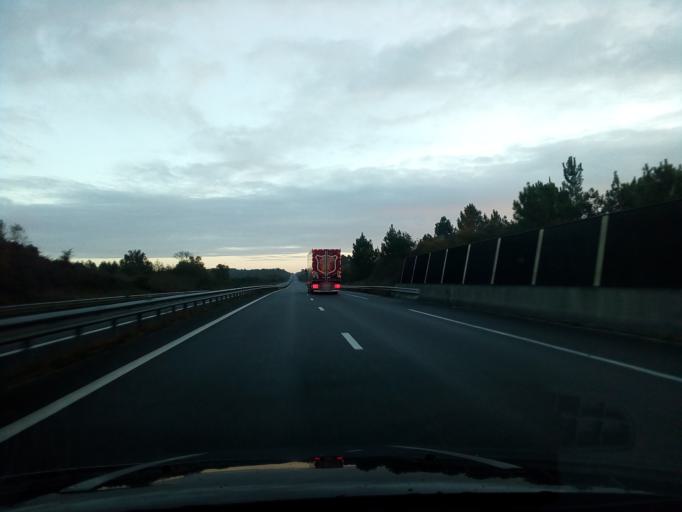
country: FR
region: Poitou-Charentes
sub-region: Departement de la Charente-Maritime
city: Montlieu-la-Garde
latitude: 45.2077
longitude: -0.2983
